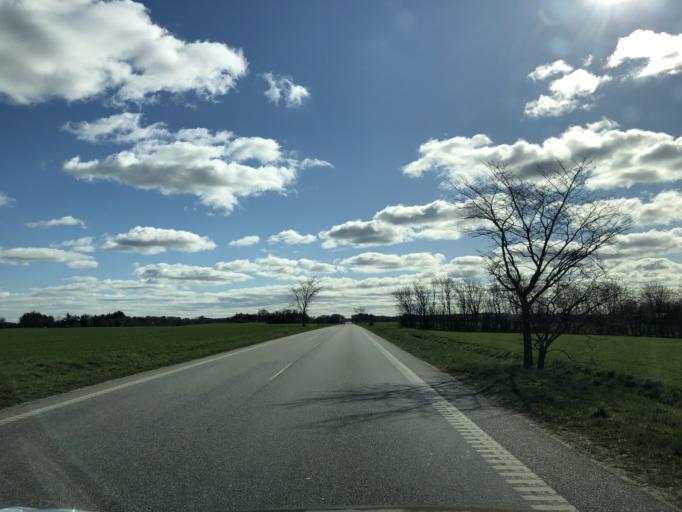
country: DK
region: North Denmark
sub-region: Vesthimmerland Kommune
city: Alestrup
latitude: 56.6147
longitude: 9.6243
